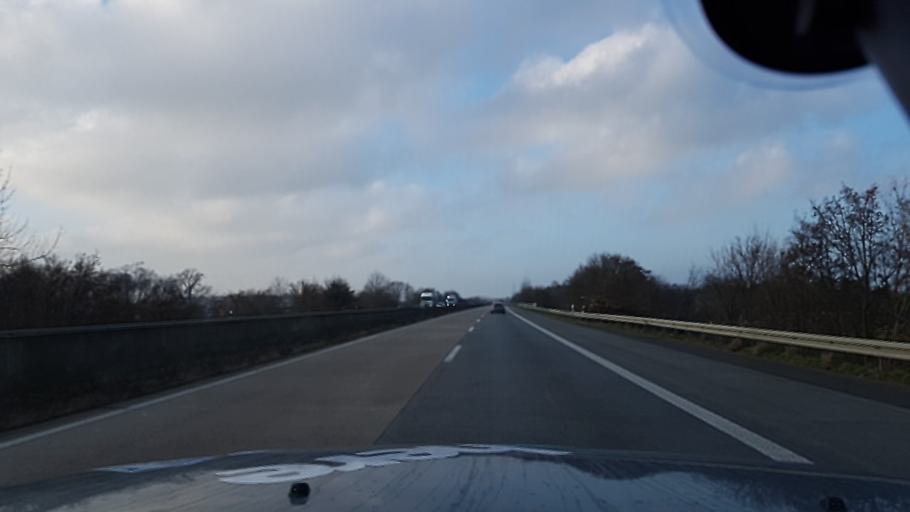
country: DE
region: North Rhine-Westphalia
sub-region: Regierungsbezirk Munster
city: Dreierwalde
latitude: 52.2952
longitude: 7.5144
